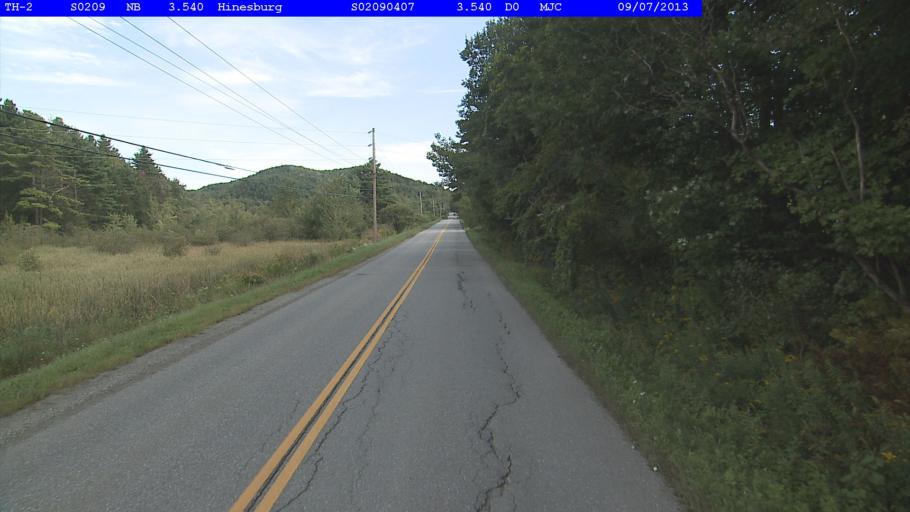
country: US
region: Vermont
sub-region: Chittenden County
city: Hinesburg
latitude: 44.3619
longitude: -73.0733
